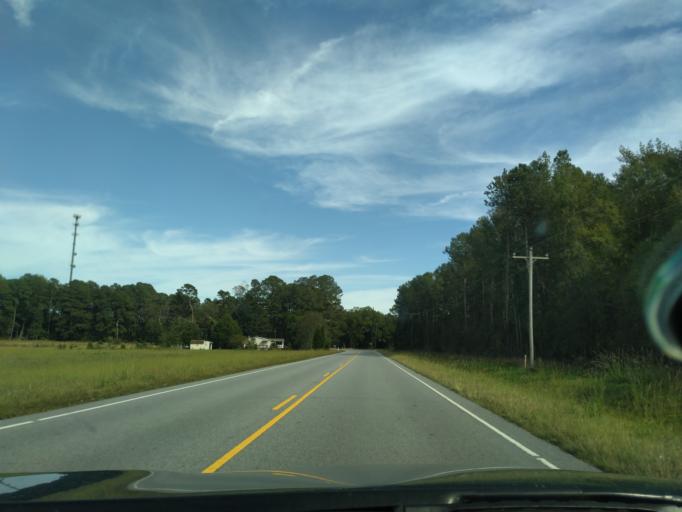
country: US
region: North Carolina
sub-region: Beaufort County
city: River Road
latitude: 35.5214
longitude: -76.8184
